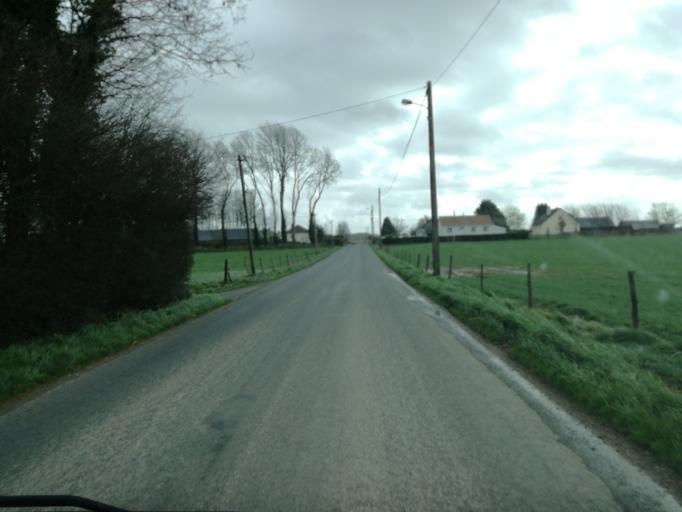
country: FR
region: Haute-Normandie
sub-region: Departement de la Seine-Maritime
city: Yebleron
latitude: 49.6636
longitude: 0.5070
